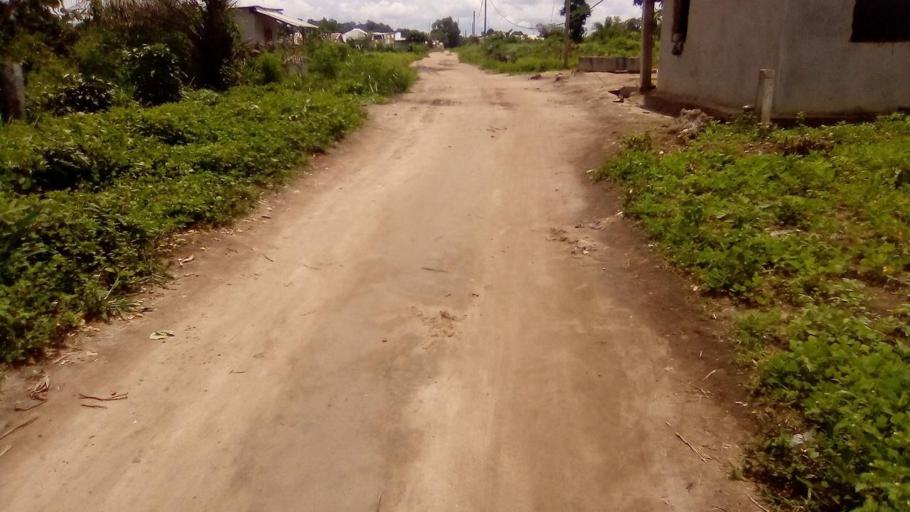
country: SL
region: Southern Province
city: Bo
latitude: 7.9354
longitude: -11.7486
